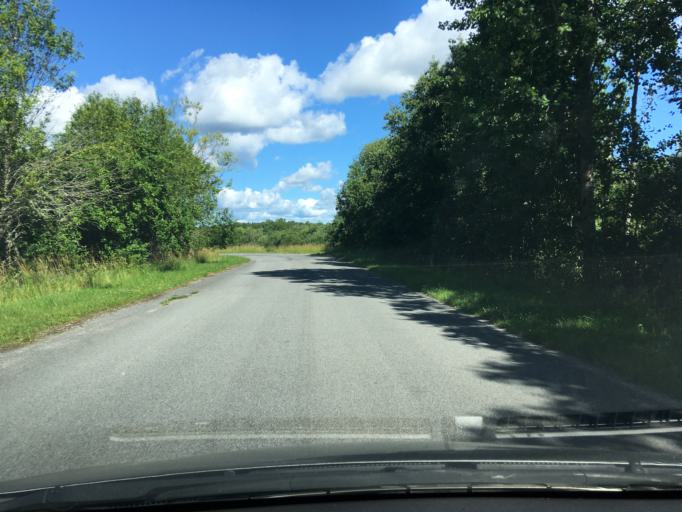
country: EE
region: Laeaene
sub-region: Lihula vald
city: Lihula
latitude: 58.7342
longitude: 23.9948
